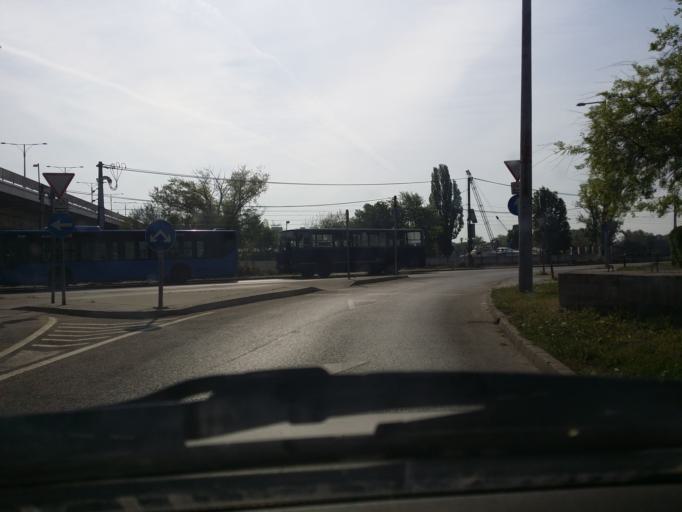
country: HU
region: Budapest
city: Budapest III. keruelet
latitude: 47.5389
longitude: 19.0466
